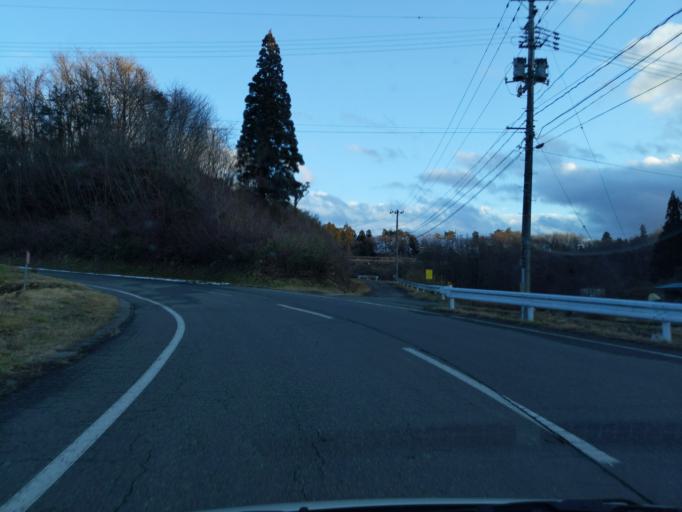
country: JP
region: Iwate
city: Ichinoseki
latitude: 38.9612
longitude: 141.0931
